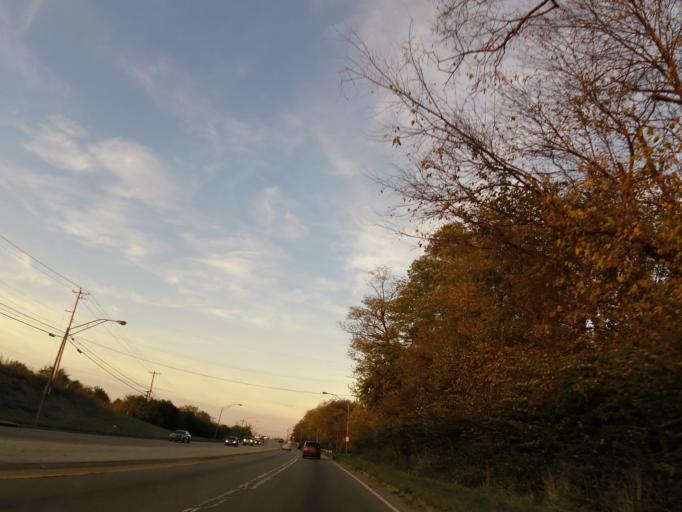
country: US
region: Kentucky
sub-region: Fayette County
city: Monticello
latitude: 37.9703
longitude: -84.5324
